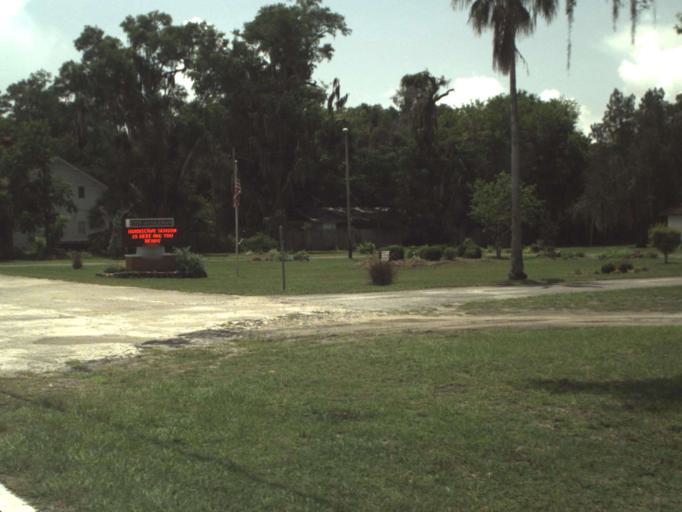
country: US
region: Florida
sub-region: Sumter County
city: Lake Panasoffkee
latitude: 28.7998
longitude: -82.0654
